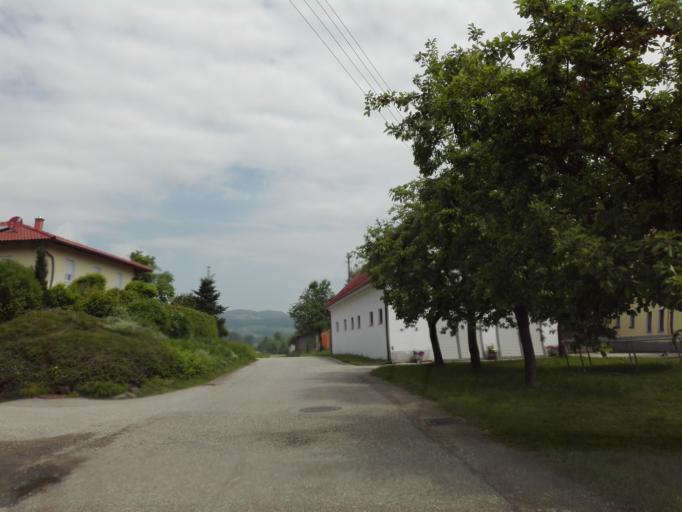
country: AT
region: Upper Austria
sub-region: Politischer Bezirk Urfahr-Umgebung
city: Feldkirchen an der Donau
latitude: 48.3584
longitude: 13.9775
